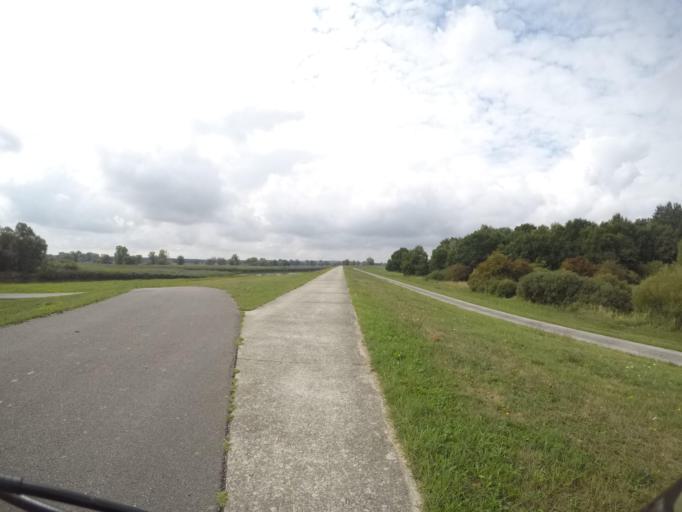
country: DE
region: Lower Saxony
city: Bleckede
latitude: 53.2980
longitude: 10.7767
